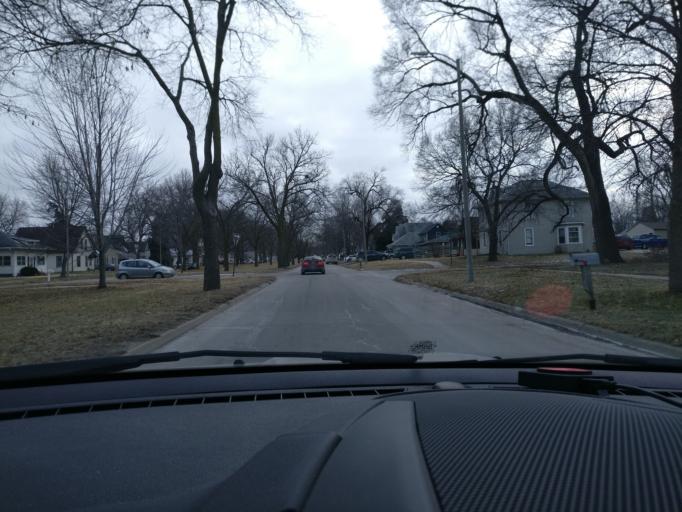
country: US
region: Nebraska
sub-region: Lancaster County
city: Lincoln
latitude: 40.8552
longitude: -96.6402
